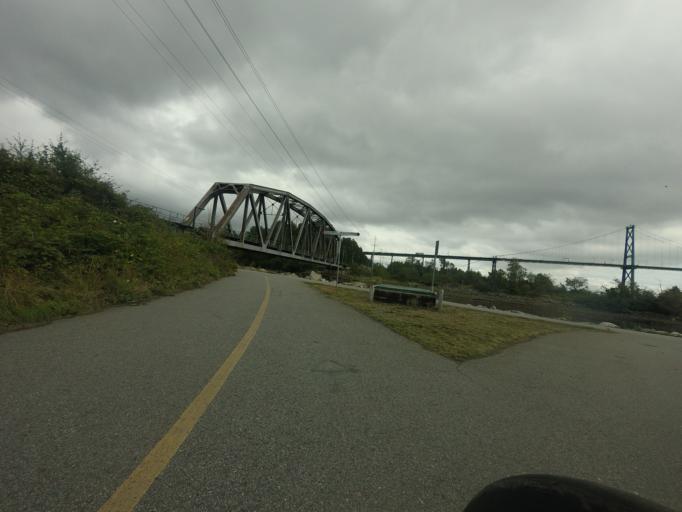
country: CA
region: British Columbia
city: West End
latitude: 49.3219
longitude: -123.1404
